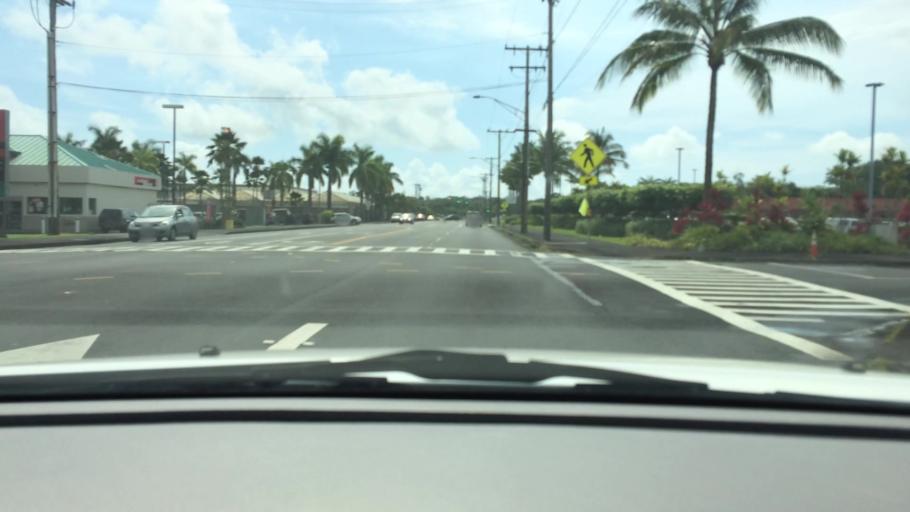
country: US
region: Hawaii
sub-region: Hawaii County
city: Hilo
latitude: 19.6992
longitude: -155.0639
